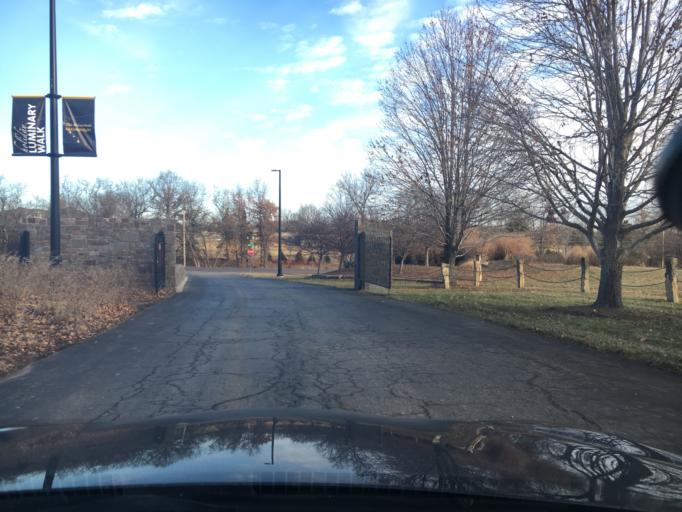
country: US
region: Kansas
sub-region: Johnson County
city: Spring Hill
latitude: 38.8028
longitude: -94.6888
